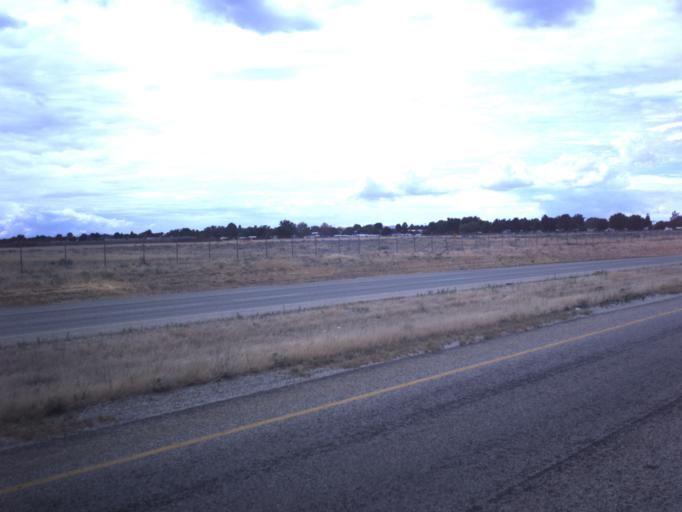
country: US
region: Utah
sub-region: Weber County
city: Riverdale
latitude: 41.2012
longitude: -112.0181
